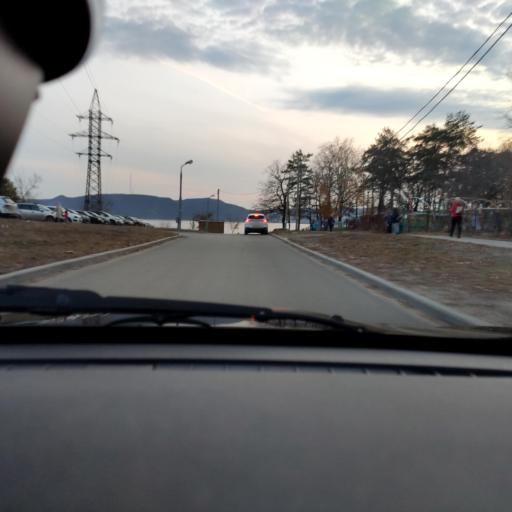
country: RU
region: Samara
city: Zhigulevsk
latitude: 53.4753
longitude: 49.4525
